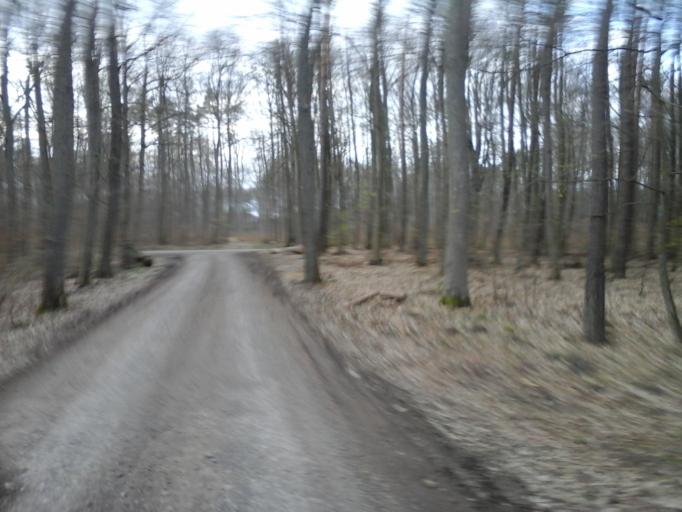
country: PL
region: West Pomeranian Voivodeship
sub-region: Powiat choszczenski
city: Bierzwnik
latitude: 53.0191
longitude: 15.6473
